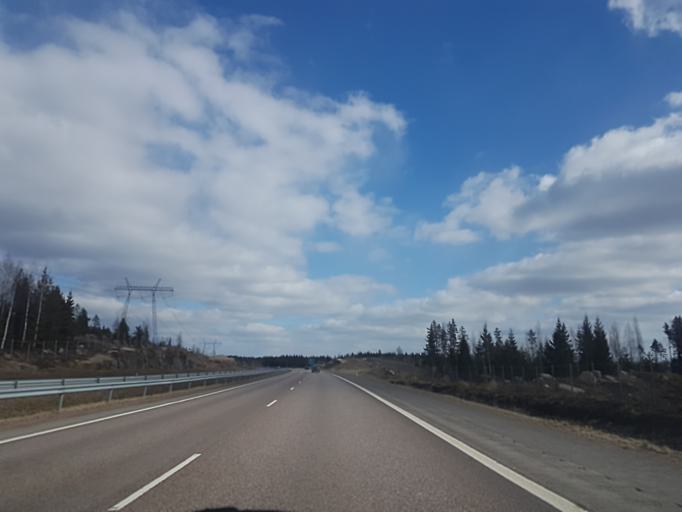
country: FI
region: Uusimaa
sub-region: Loviisa
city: Ruotsinpyhtaeae
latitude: 60.4871
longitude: 26.3760
